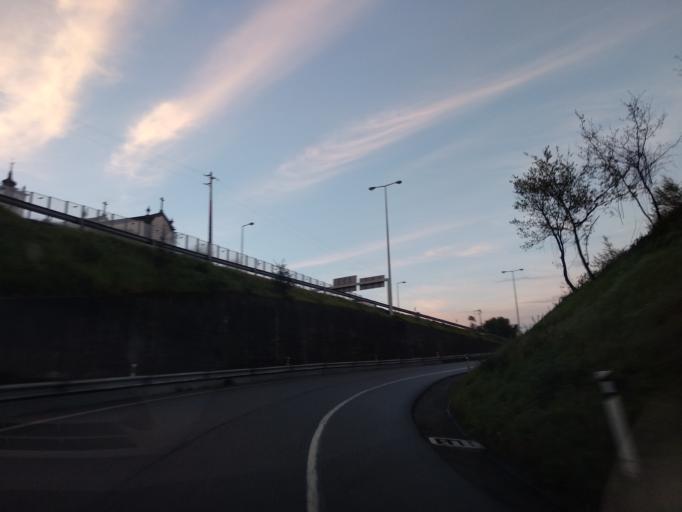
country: PT
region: Braga
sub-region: Vila Nova de Famalicao
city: Vila Nova de Famalicao
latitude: 41.3753
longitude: -8.5030
